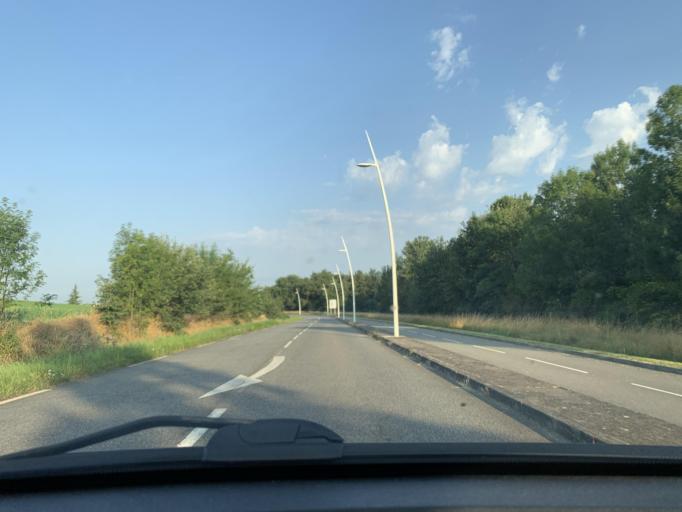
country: FR
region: Midi-Pyrenees
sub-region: Departement de la Haute-Garonne
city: Labege
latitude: 43.5349
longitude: 1.5408
